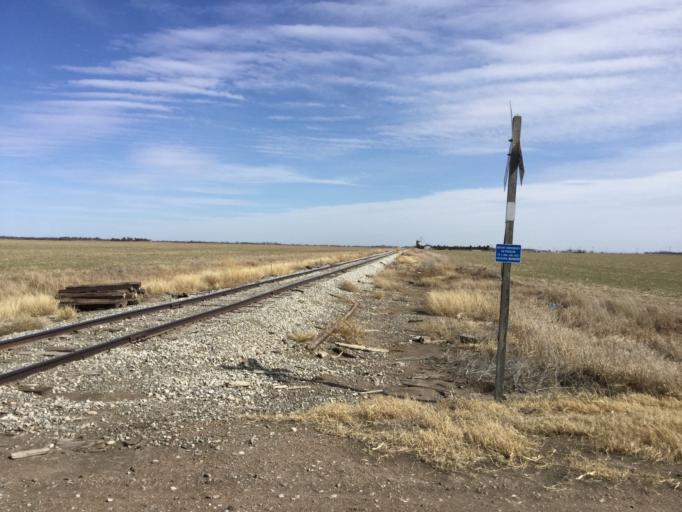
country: US
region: Kansas
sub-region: Edwards County
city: Kinsley
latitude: 38.1930
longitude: -99.3873
